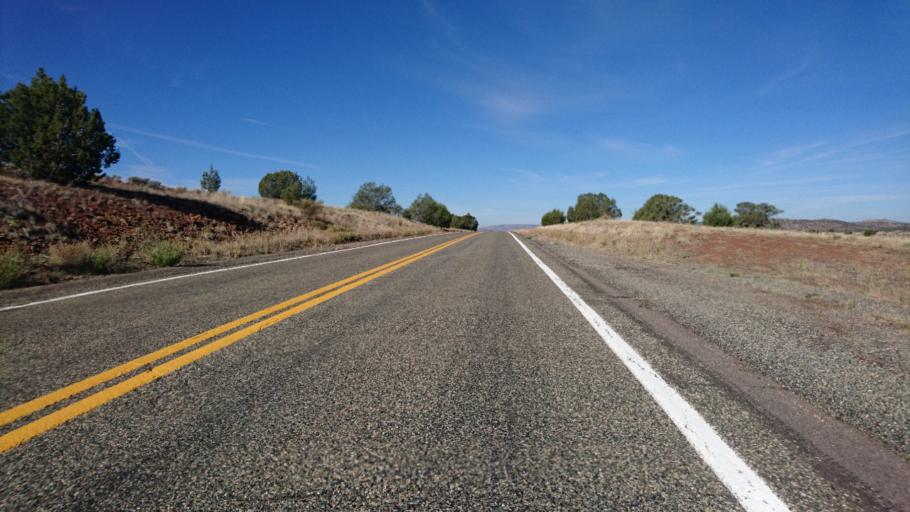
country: US
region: Arizona
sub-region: Yavapai County
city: Paulden
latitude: 35.2815
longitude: -112.7089
